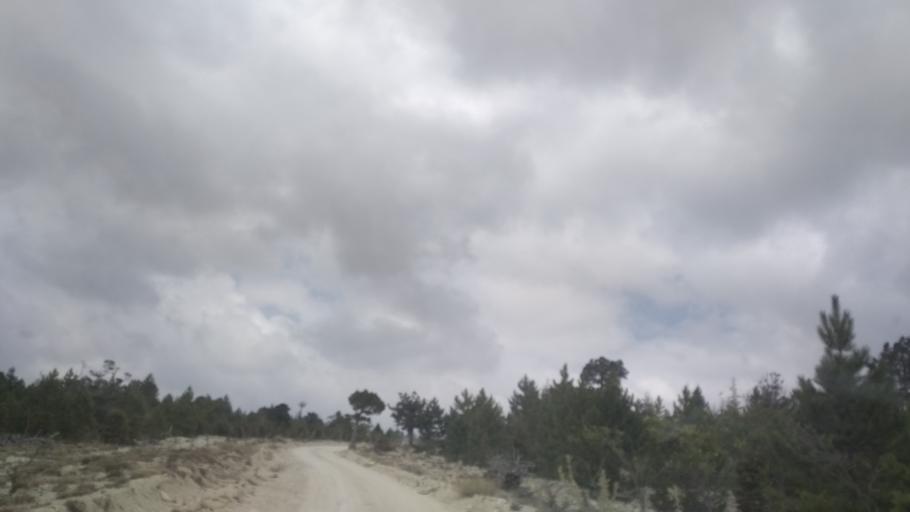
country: TR
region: Mersin
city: Sarikavak
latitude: 36.5732
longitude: 33.7610
